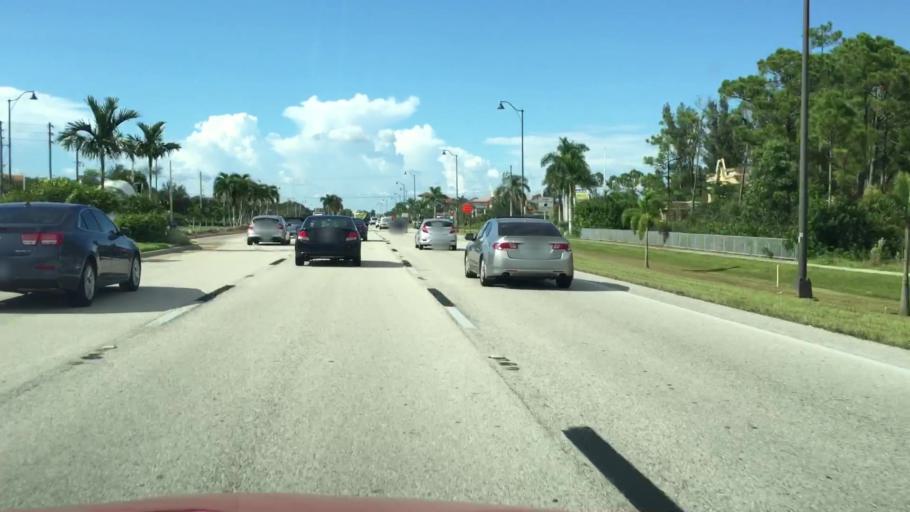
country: US
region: Florida
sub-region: Lee County
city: Estero
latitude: 26.3859
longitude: -81.8104
